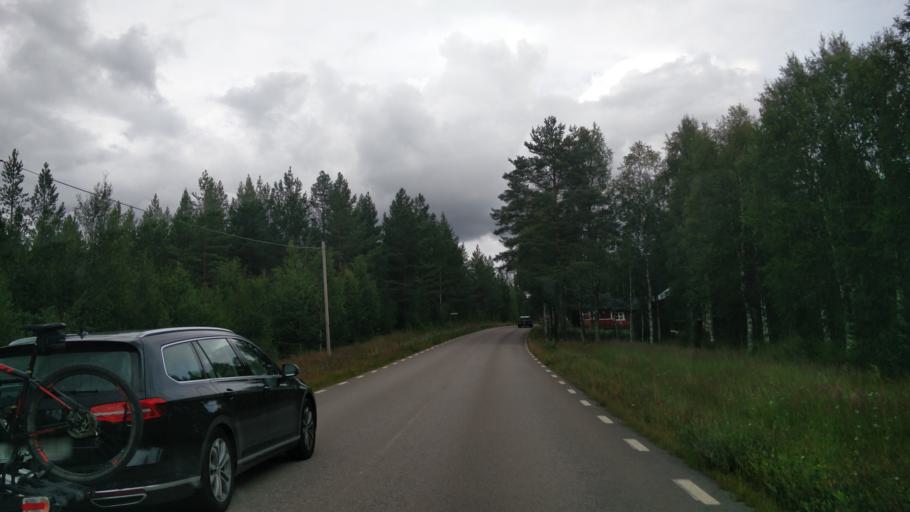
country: NO
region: Hedmark
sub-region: Trysil
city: Innbygda
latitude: 61.1682
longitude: 12.8385
